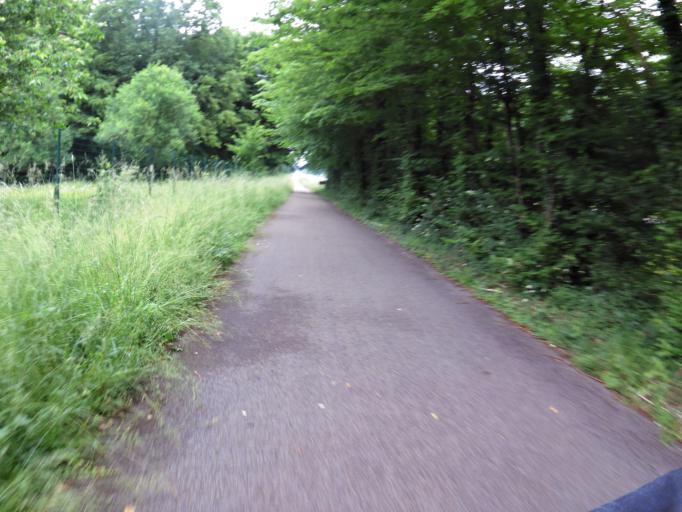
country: FR
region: Champagne-Ardenne
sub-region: Departement de la Haute-Marne
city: Laneuville-a-Remy
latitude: 48.5585
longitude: 4.8403
